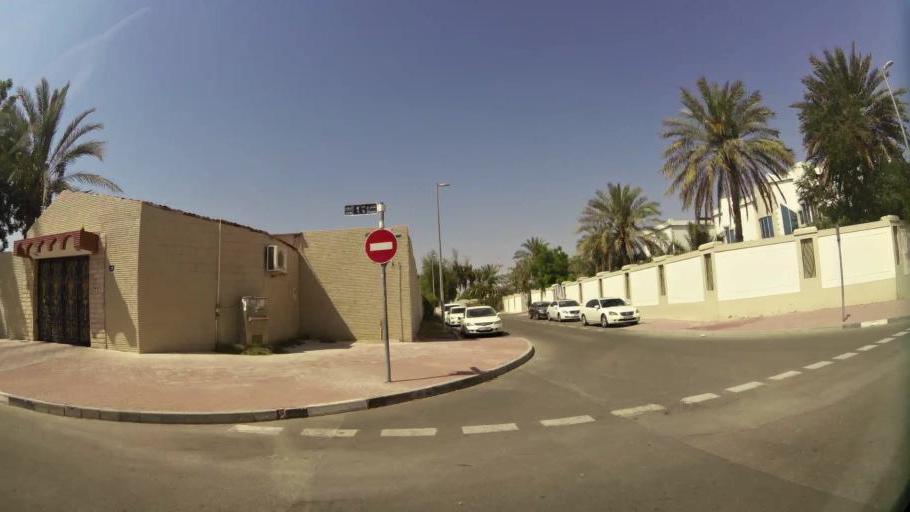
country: AE
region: Ash Shariqah
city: Sharjah
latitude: 25.2678
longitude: 55.3654
